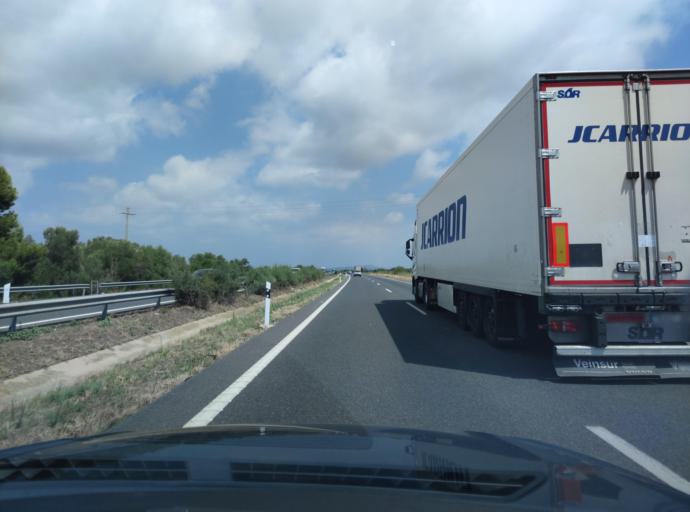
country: ES
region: Valencia
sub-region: Provincia de Castello
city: Vinaros
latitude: 40.4981
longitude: 0.4158
